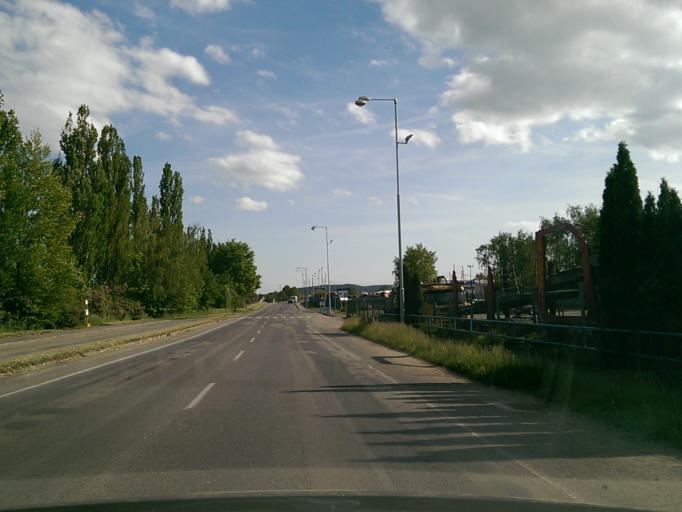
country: CZ
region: Central Bohemia
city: Mnichovo Hradiste
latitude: 50.5074
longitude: 14.9690
